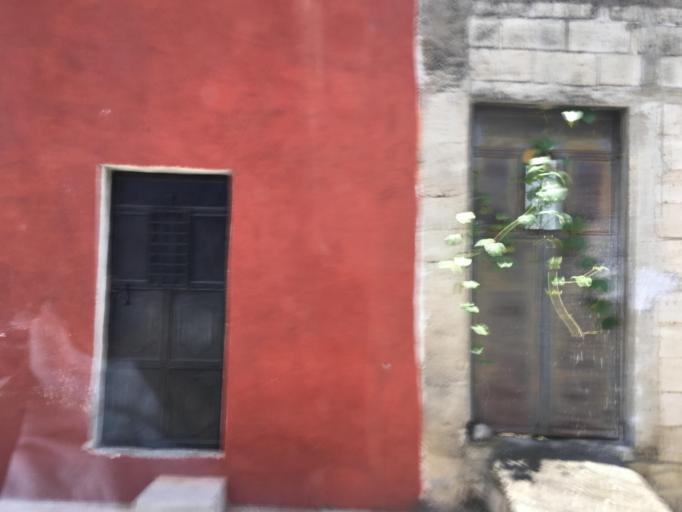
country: GT
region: Sacatepequez
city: Antigua Guatemala
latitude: 14.5498
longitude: -90.7308
